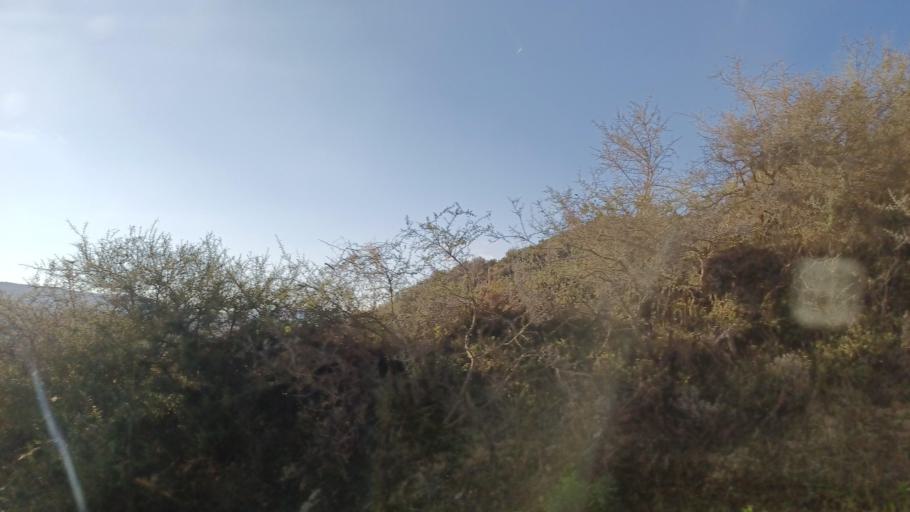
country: CY
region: Limassol
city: Pachna
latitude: 34.8558
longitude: 32.7238
